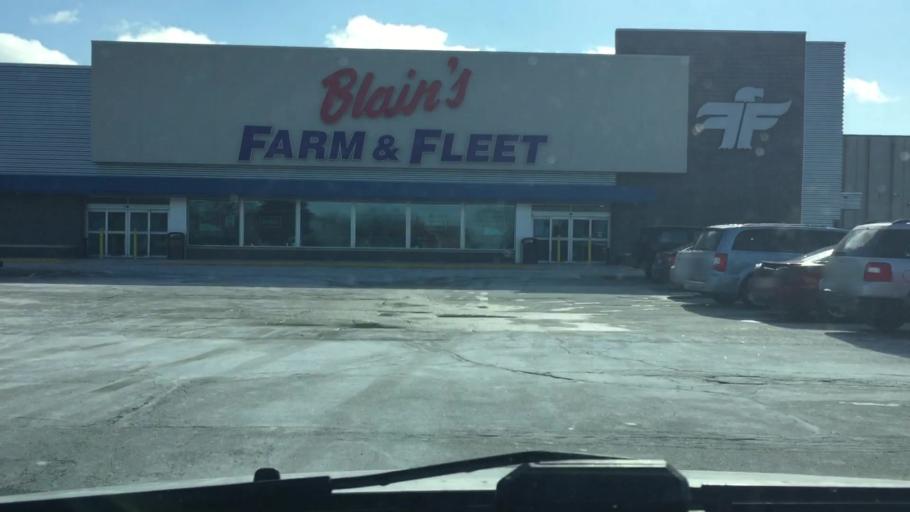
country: US
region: Wisconsin
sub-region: Milwaukee County
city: South Milwaukee
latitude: 42.9156
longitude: -87.9182
